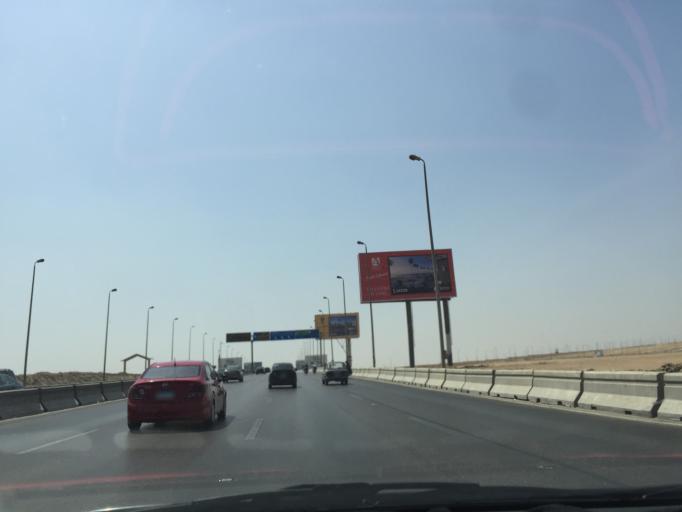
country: EG
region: Al Jizah
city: Awsim
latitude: 30.0525
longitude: 31.0660
